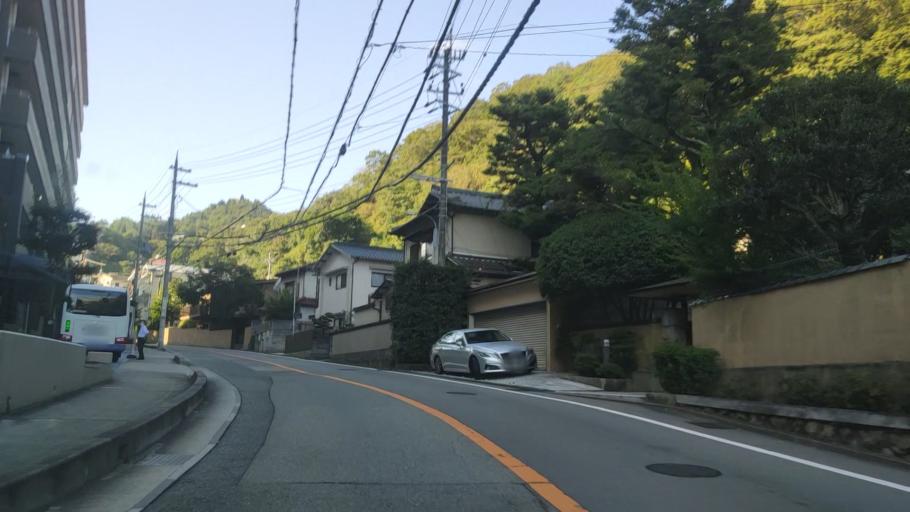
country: JP
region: Hyogo
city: Sandacho
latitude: 34.8018
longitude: 135.2470
